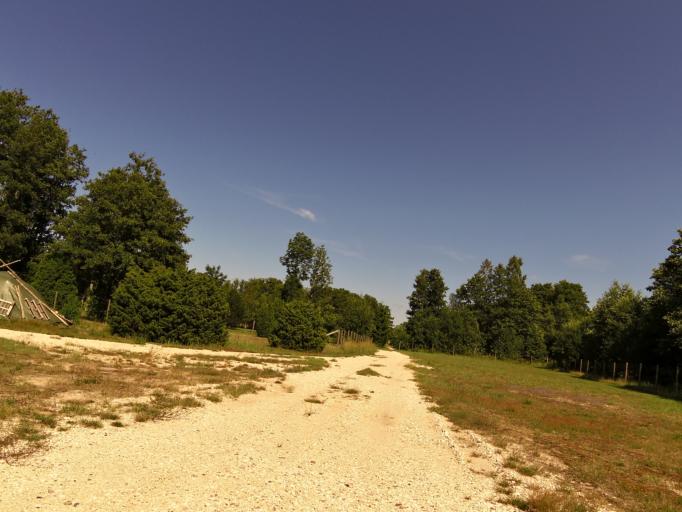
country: EE
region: Hiiumaa
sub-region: Kaerdla linn
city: Kardla
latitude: 58.7770
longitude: 22.4846
